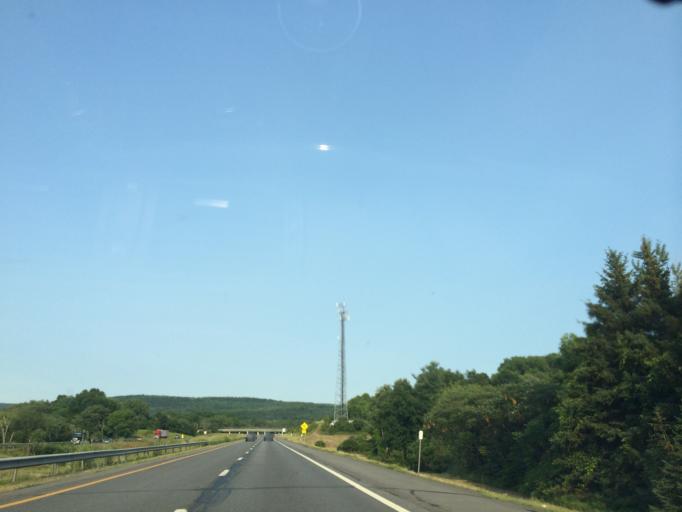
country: US
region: New York
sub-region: Rensselaer County
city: Nassau
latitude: 42.4625
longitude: -73.5998
